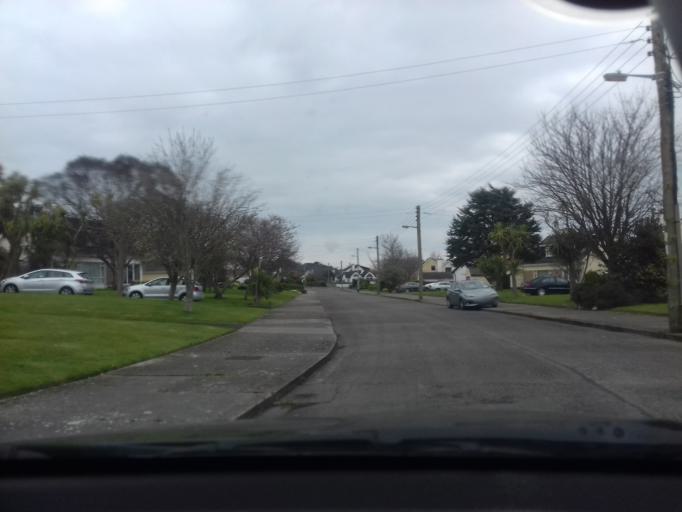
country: IE
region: Leinster
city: Sutton
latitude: 53.3861
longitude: -6.0964
